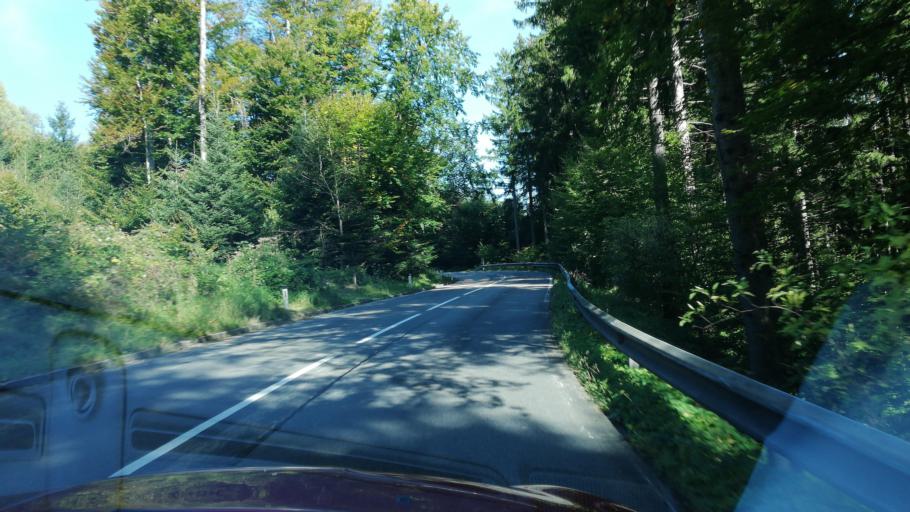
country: AT
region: Upper Austria
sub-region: Politischer Bezirk Vocklabruck
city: Redleiten
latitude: 48.1103
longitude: 13.5653
